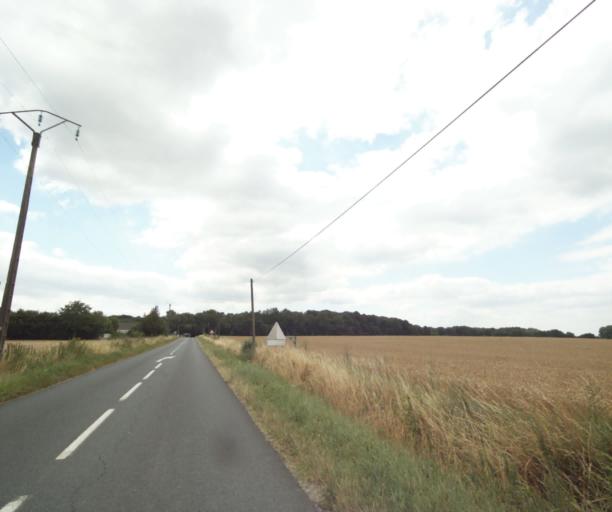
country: FR
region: Centre
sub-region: Departement du Loiret
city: Boigny-sur-Bionne
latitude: 47.9241
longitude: 2.0243
